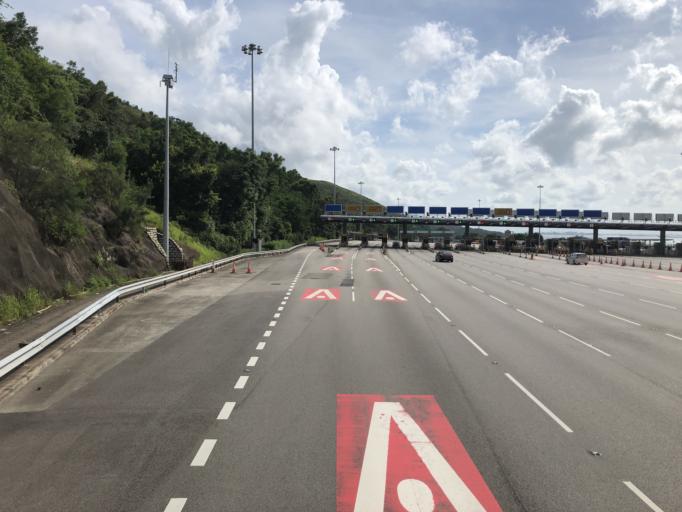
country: HK
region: Tsuen Wan
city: Tsuen Wan
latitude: 22.3396
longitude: 114.0445
